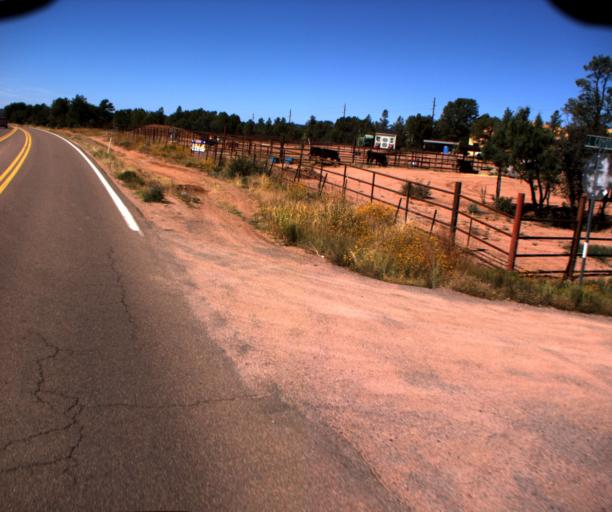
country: US
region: Arizona
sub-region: Gila County
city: Star Valley
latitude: 34.2644
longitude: -111.2241
